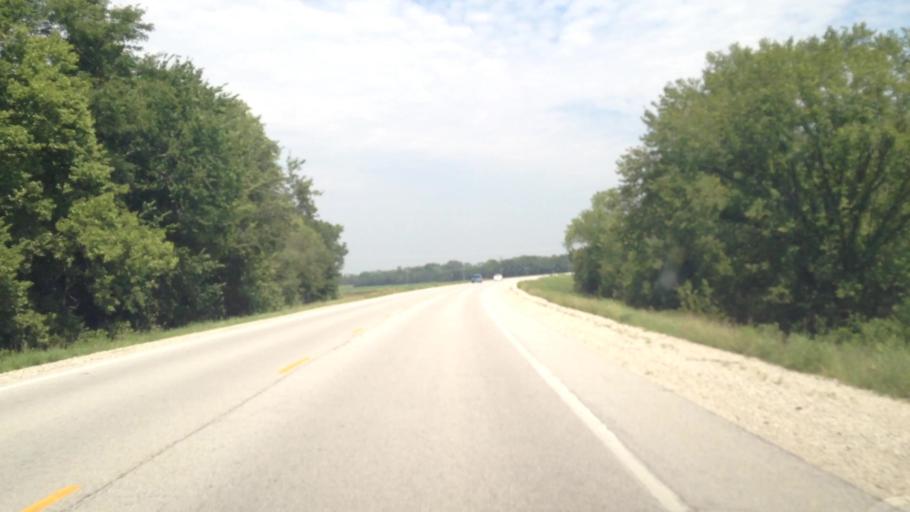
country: US
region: Kansas
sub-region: Neosho County
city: Erie
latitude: 37.5417
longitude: -95.2694
